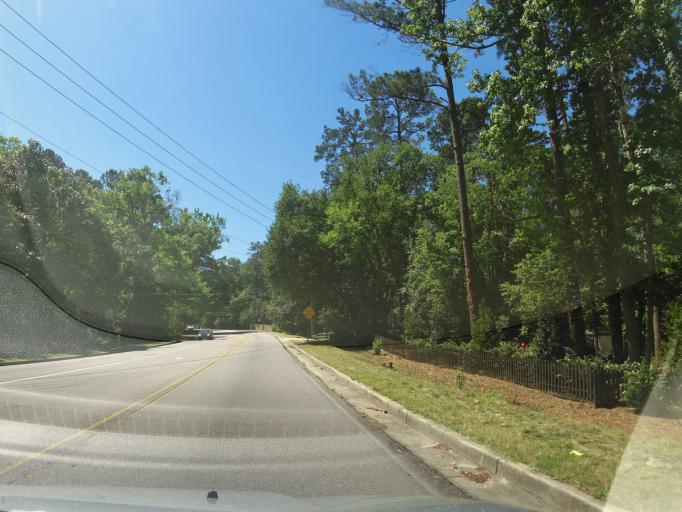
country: US
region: Georgia
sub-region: Columbia County
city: Martinez
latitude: 33.4938
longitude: -82.0304
